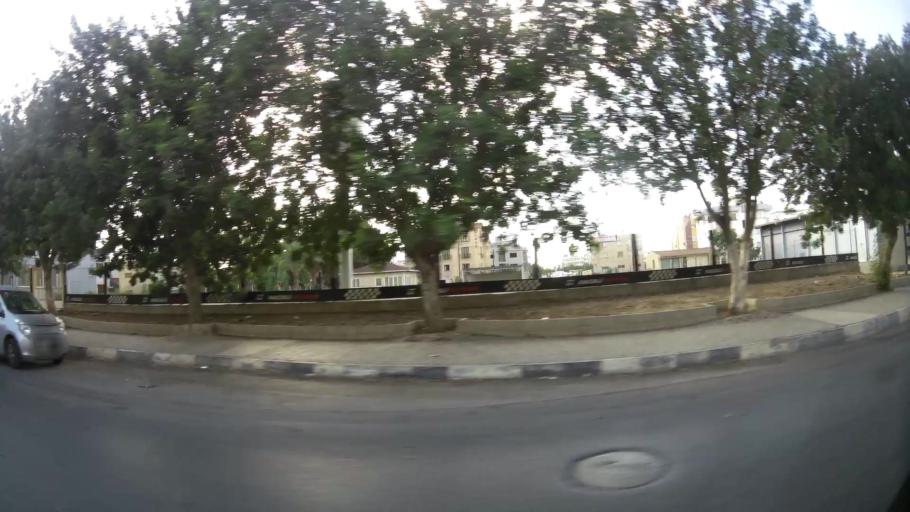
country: CY
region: Lefkosia
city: Nicosia
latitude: 35.2010
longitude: 33.3673
